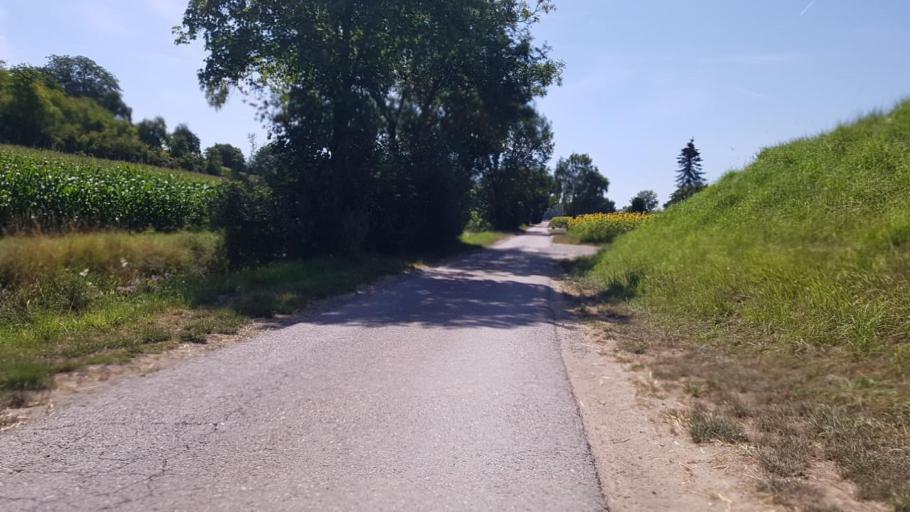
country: DE
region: Baden-Wuerttemberg
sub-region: Karlsruhe Region
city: Sulzfeld
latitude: 49.1665
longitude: 8.8537
